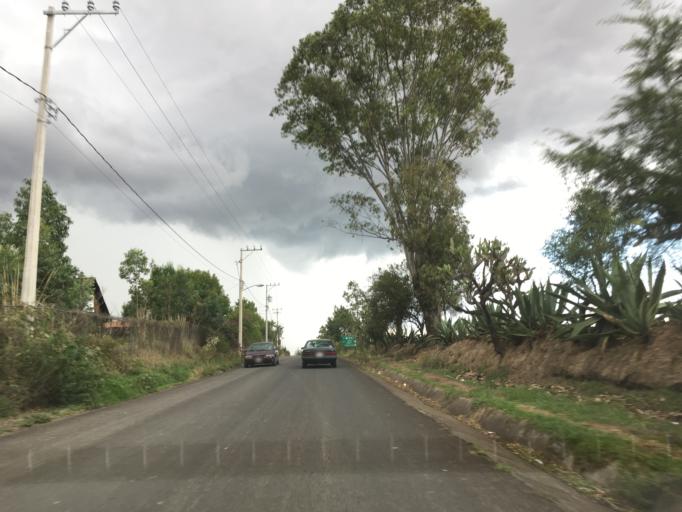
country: MX
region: Michoacan
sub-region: Morelia
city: La Mintzita (Piedra Dura)
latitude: 19.5933
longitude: -101.2737
